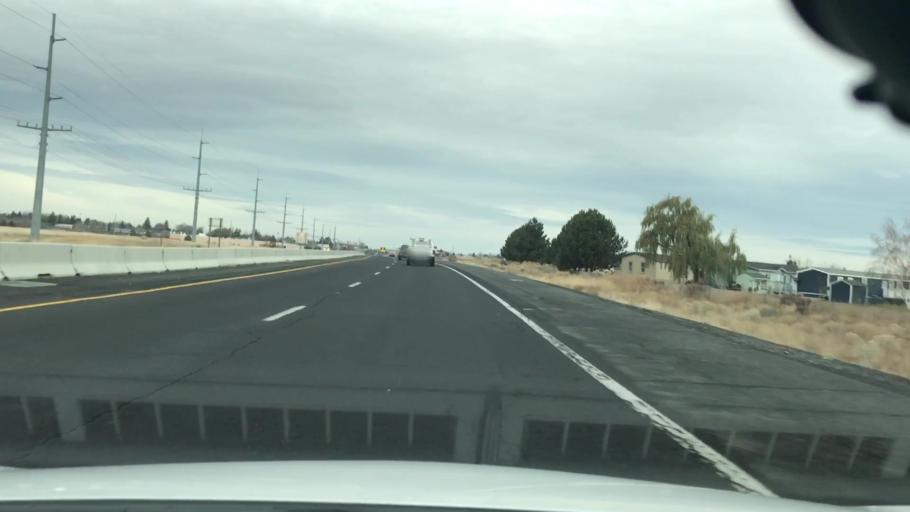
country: US
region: Washington
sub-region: Grant County
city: Moses Lake
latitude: 47.1461
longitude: -119.2853
